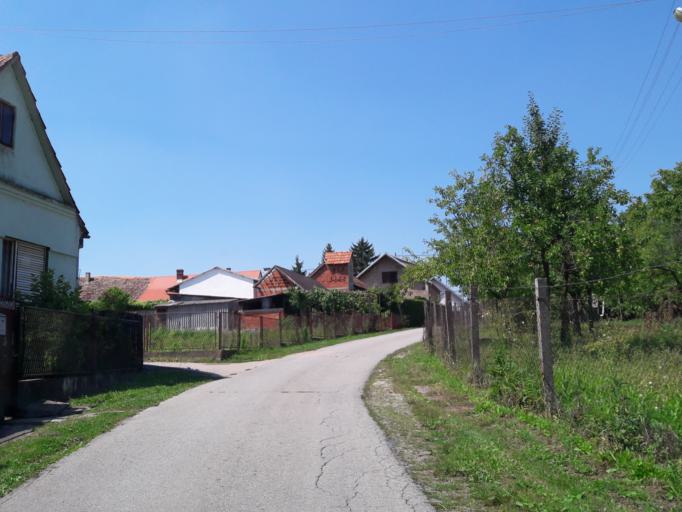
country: HR
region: Vukovarsko-Srijemska
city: Vodinci
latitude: 45.2855
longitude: 18.5607
